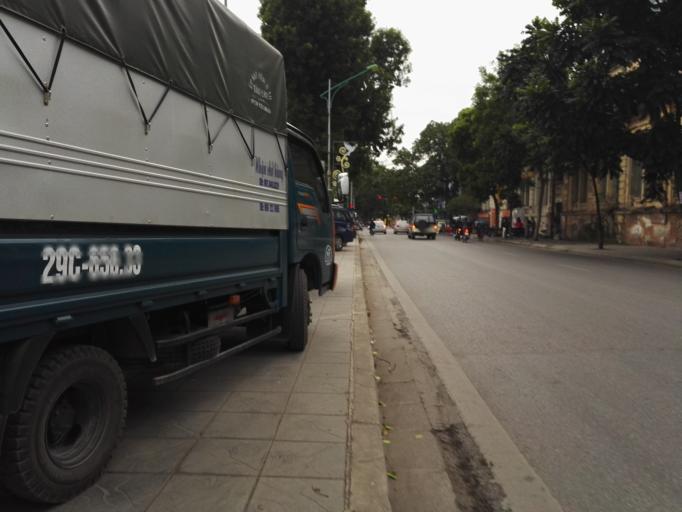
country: VN
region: Ha Noi
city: Hoan Kiem
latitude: 21.0472
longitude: 105.8431
